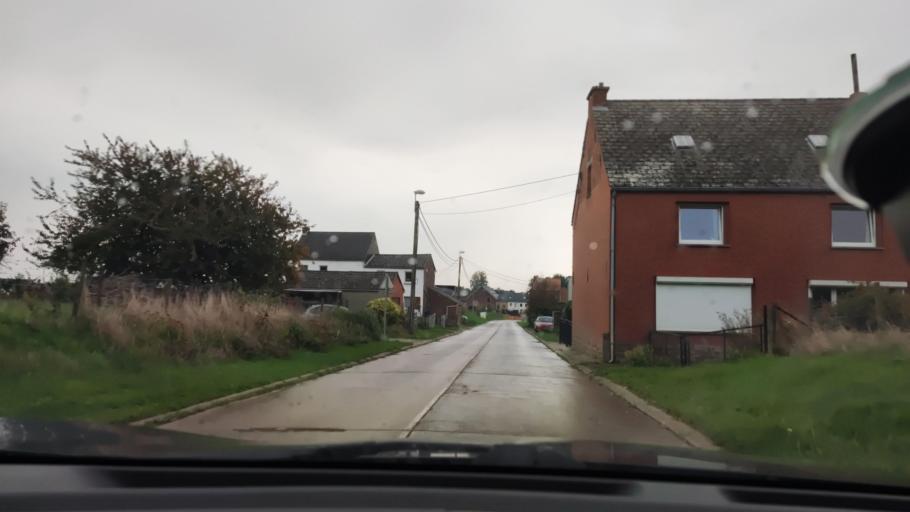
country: BE
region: Wallonia
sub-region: Province du Brabant Wallon
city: Jodoigne
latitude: 50.7286
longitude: 4.9117
